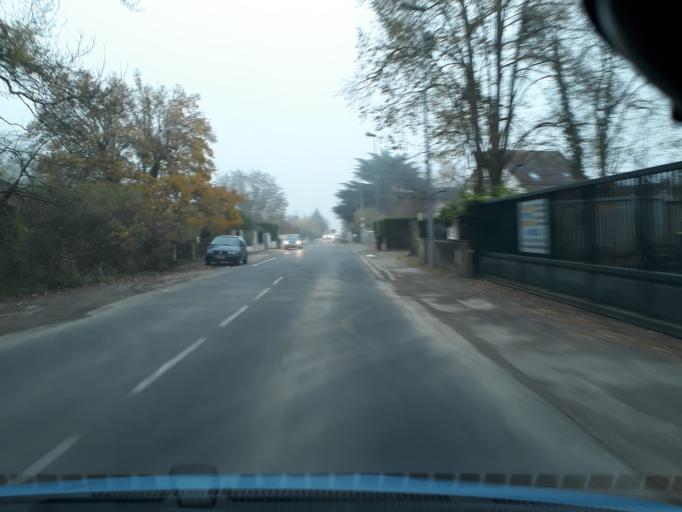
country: FR
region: Ile-de-France
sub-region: Departement de Seine-et-Marne
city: Veneux-les-Sablons
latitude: 48.3867
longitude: 2.7795
